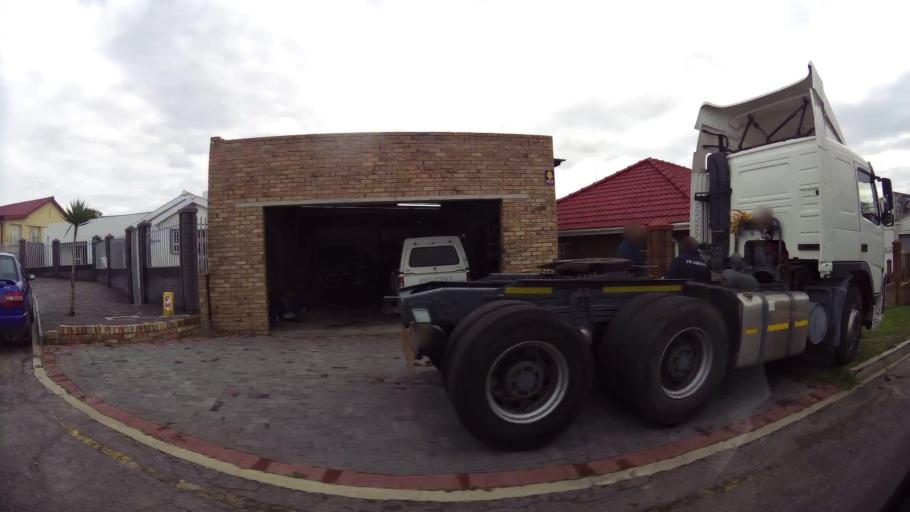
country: ZA
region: Eastern Cape
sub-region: Nelson Mandela Bay Metropolitan Municipality
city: Port Elizabeth
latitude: -33.9389
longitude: 25.5872
